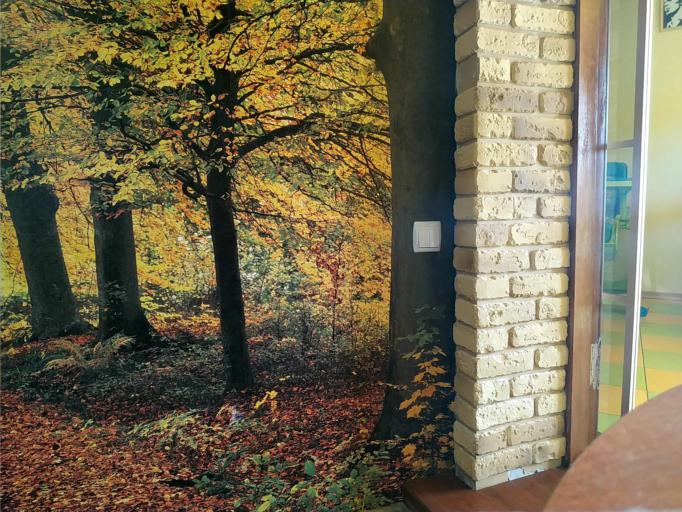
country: RU
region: Smolensk
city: Katyn'
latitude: 54.9924
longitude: 31.7456
